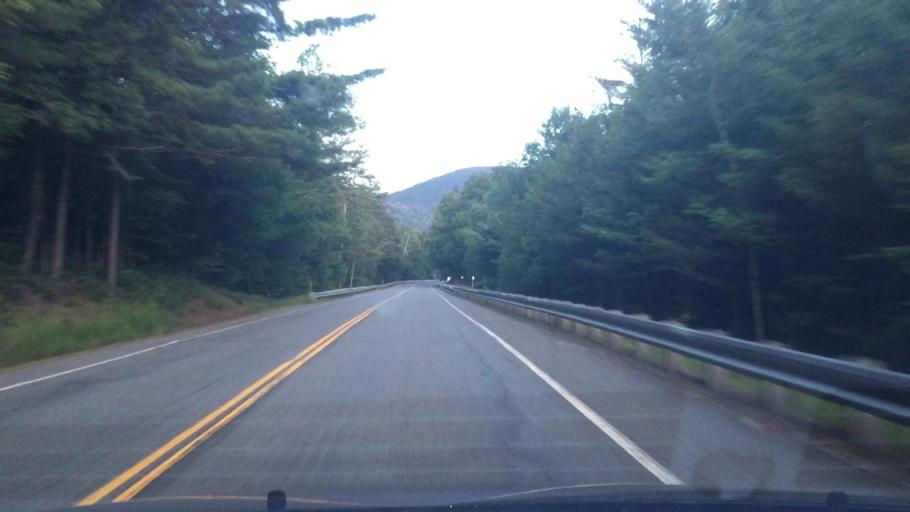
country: US
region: New Hampshire
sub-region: Grafton County
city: Woodstock
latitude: 44.0362
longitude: -71.5307
